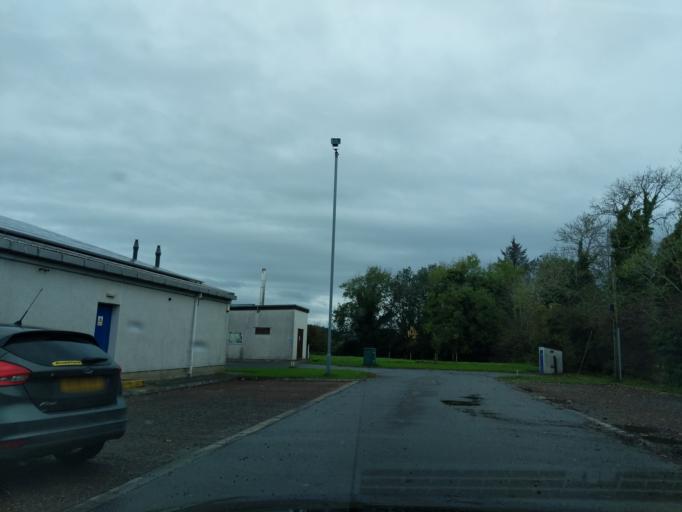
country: GB
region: Scotland
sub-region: Dumfries and Galloway
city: Kirkcudbright
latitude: 54.8360
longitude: -4.0586
